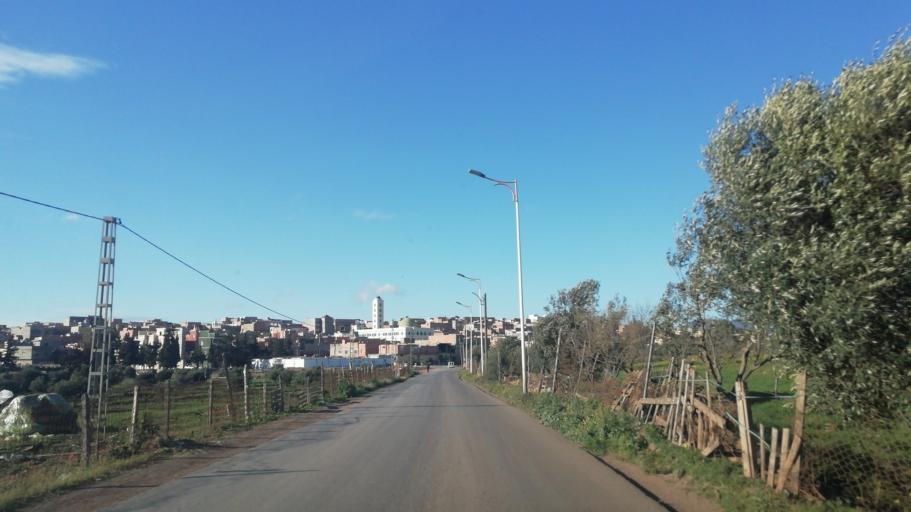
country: DZ
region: Oran
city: Sidi ech Chahmi
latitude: 35.6871
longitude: -0.4954
